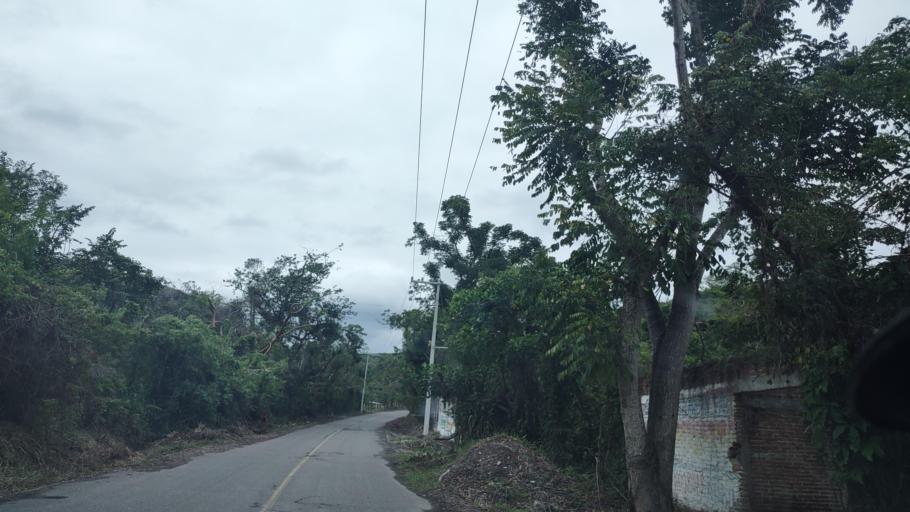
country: MX
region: Veracruz
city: Papantla de Olarte
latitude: 20.4447
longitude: -97.2935
